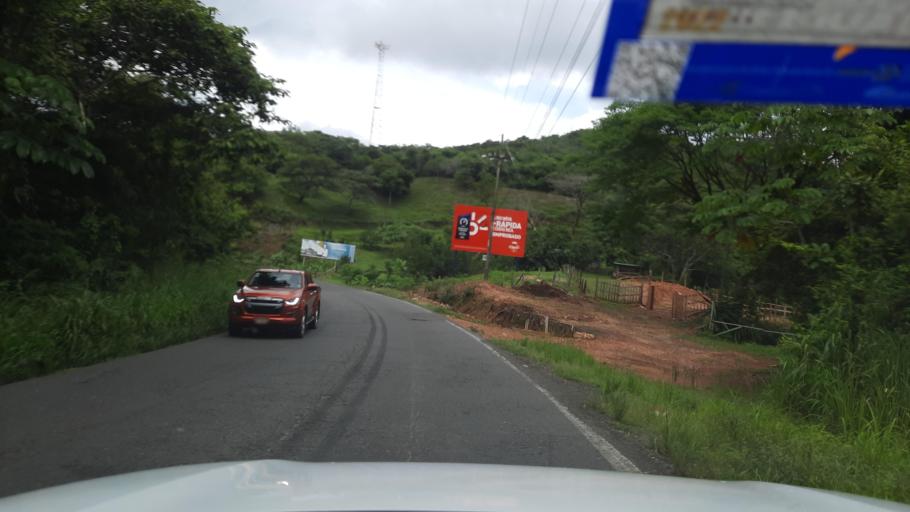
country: CR
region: Puntarenas
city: Esparza
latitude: 10.0187
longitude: -84.6096
